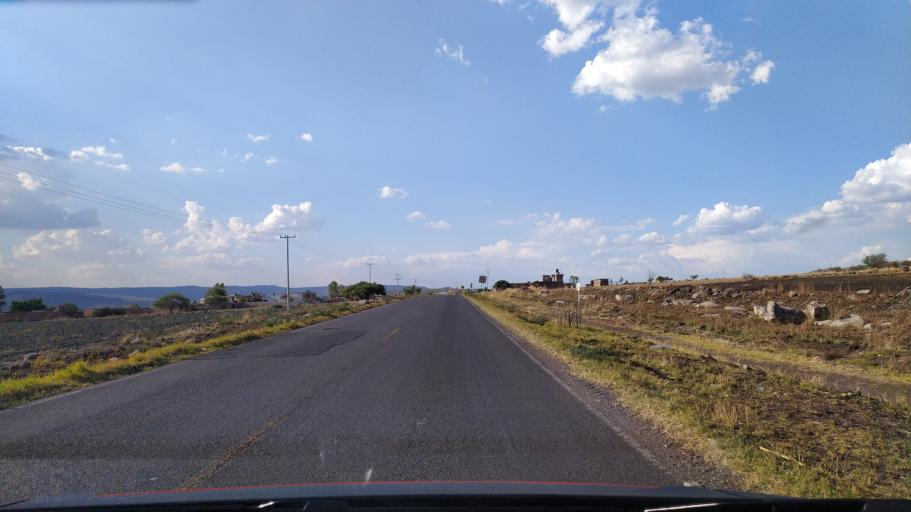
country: MX
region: Guanajuato
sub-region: Penjamo
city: Estacion la Piedad
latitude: 20.4048
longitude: -101.9986
